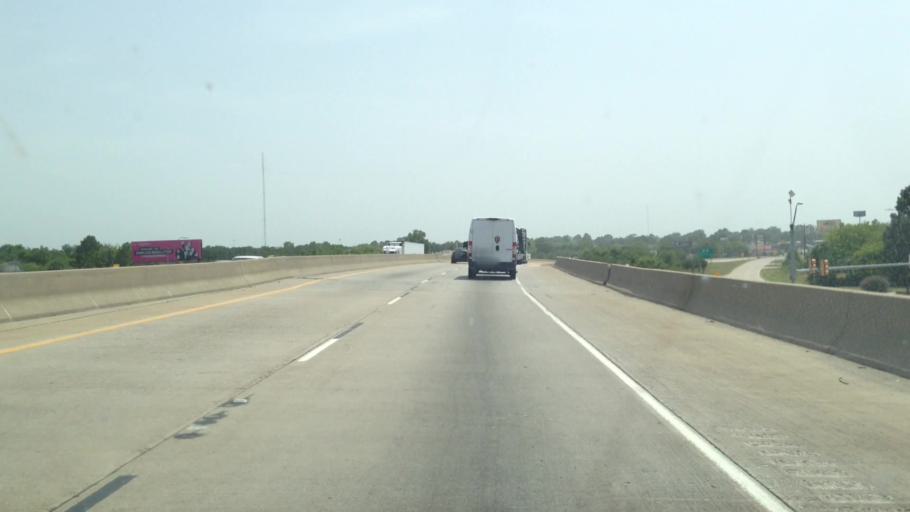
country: US
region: Texas
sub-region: Hopkins County
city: Sulphur Springs
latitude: 33.1208
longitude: -95.5849
